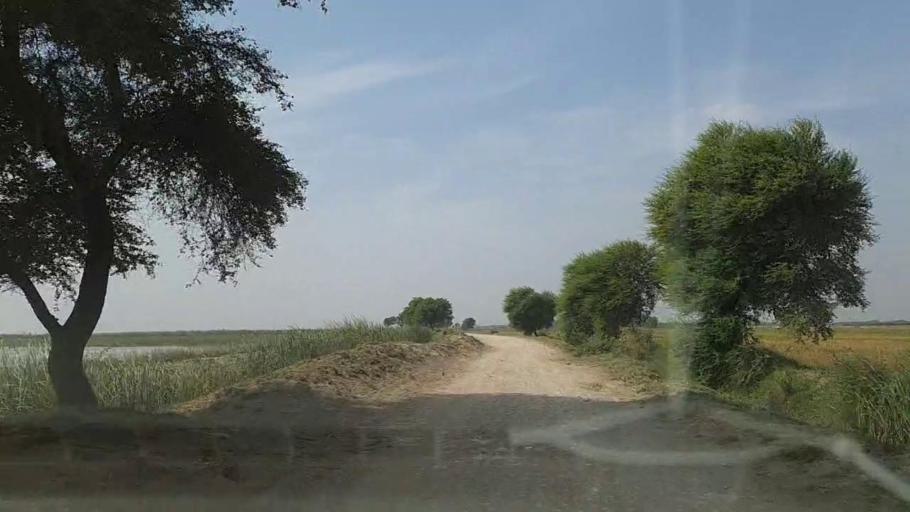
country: PK
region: Sindh
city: Mirpur Batoro
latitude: 24.6113
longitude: 68.2294
